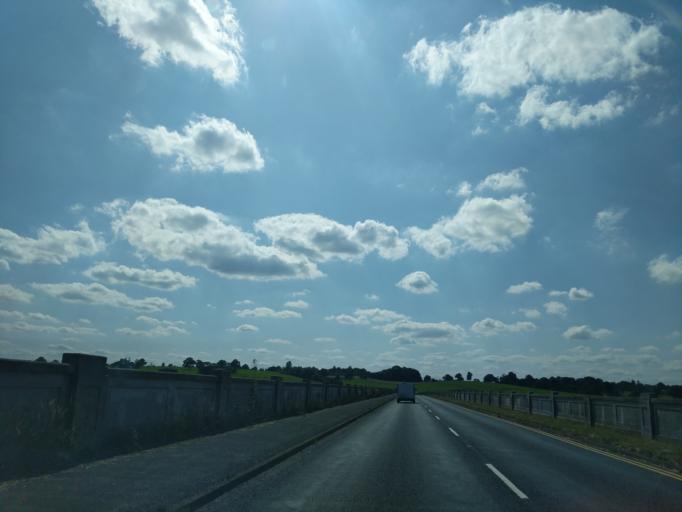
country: GB
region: England
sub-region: Staffordshire
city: Rugeley
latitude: 52.8124
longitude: -1.9125
